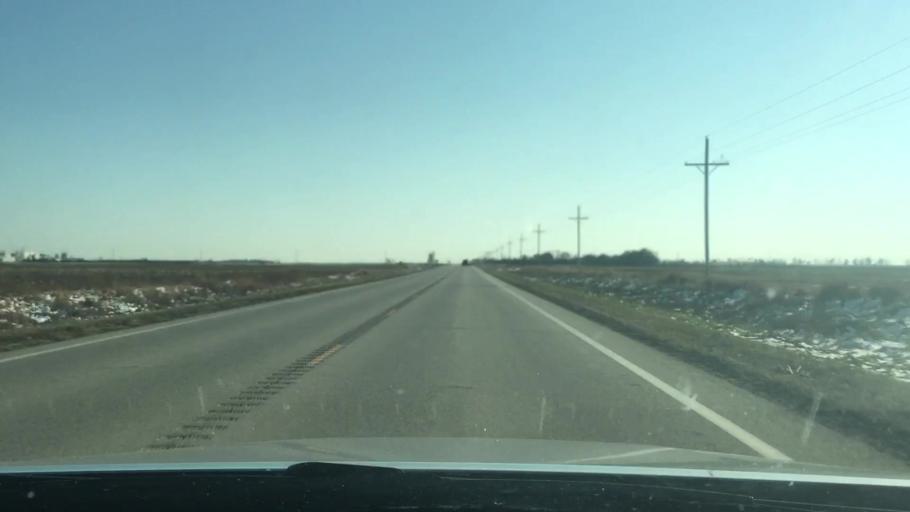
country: US
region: Kansas
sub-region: Rice County
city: Lyons
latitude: 38.2957
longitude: -98.2021
